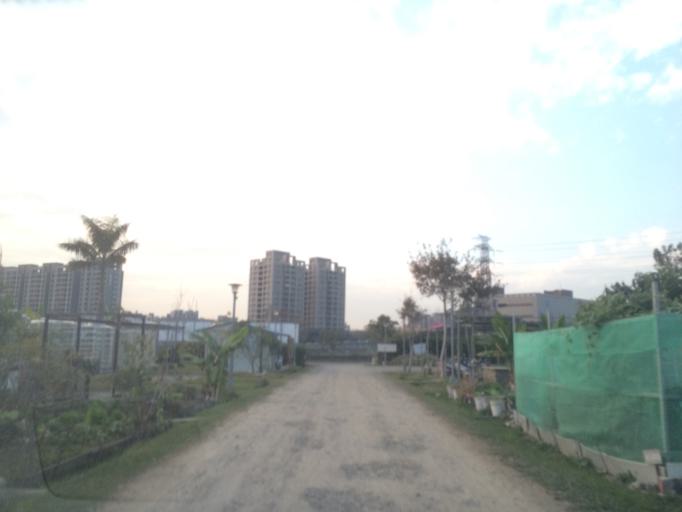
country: TW
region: Taiwan
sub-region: Taichung City
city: Taichung
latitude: 24.1584
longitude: 120.7304
